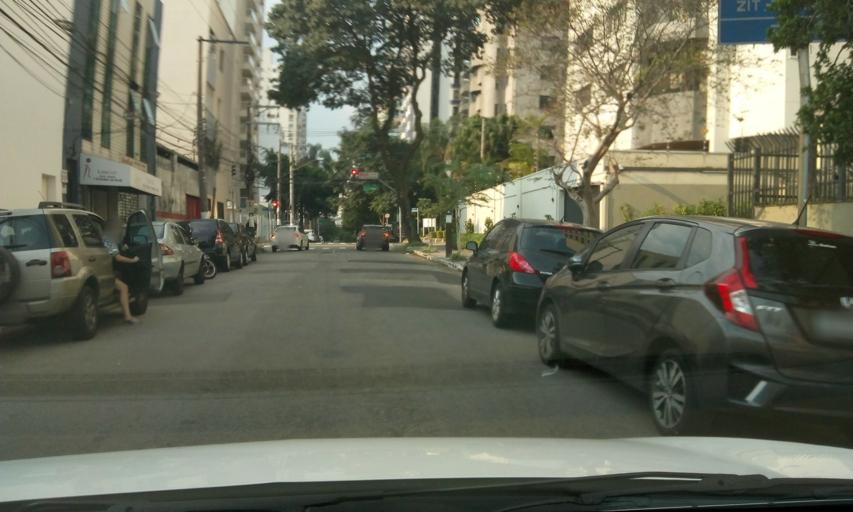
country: BR
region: Sao Paulo
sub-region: Sao Paulo
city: Sao Paulo
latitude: -23.6026
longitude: -46.6741
